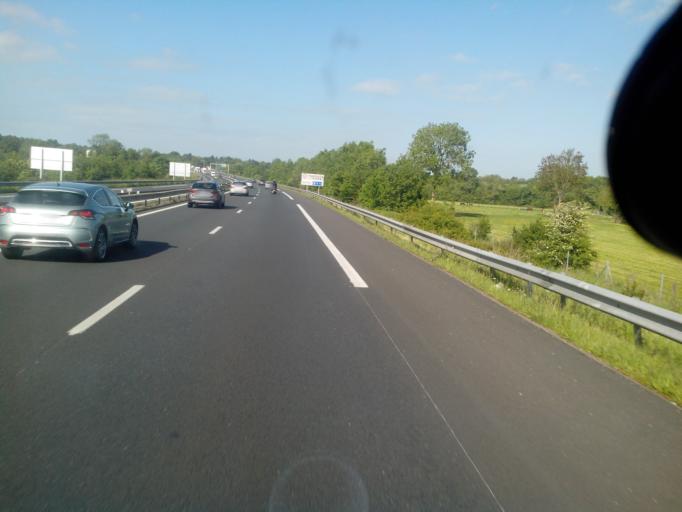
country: FR
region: Lower Normandy
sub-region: Departement du Calvados
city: Sannerville
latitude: 49.1734
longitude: -0.2086
